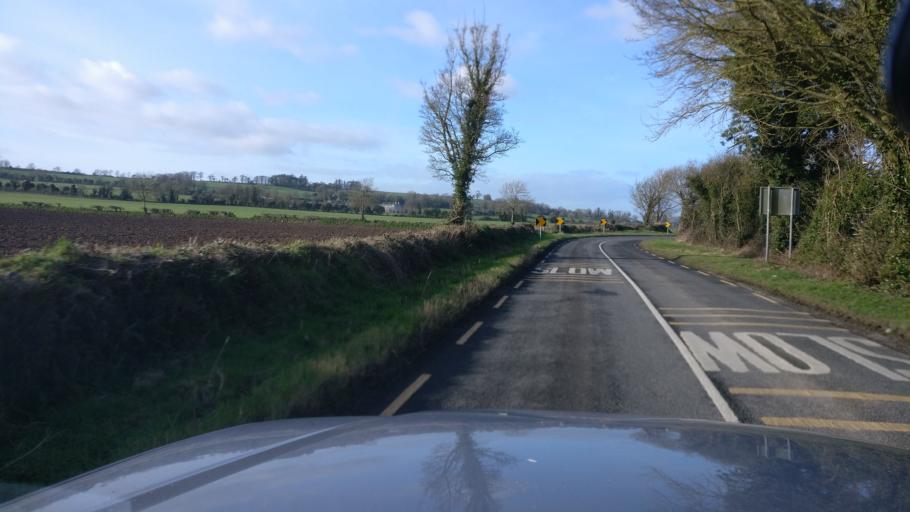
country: IE
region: Leinster
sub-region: Laois
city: Stradbally
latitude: 52.9978
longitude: -7.2239
